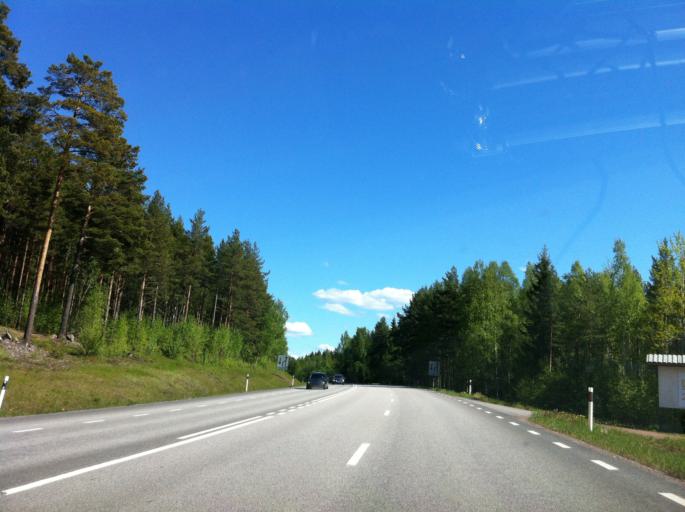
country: SE
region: Dalarna
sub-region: Rattviks Kommun
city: Vikarbyn
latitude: 60.9108
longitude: 15.0552
